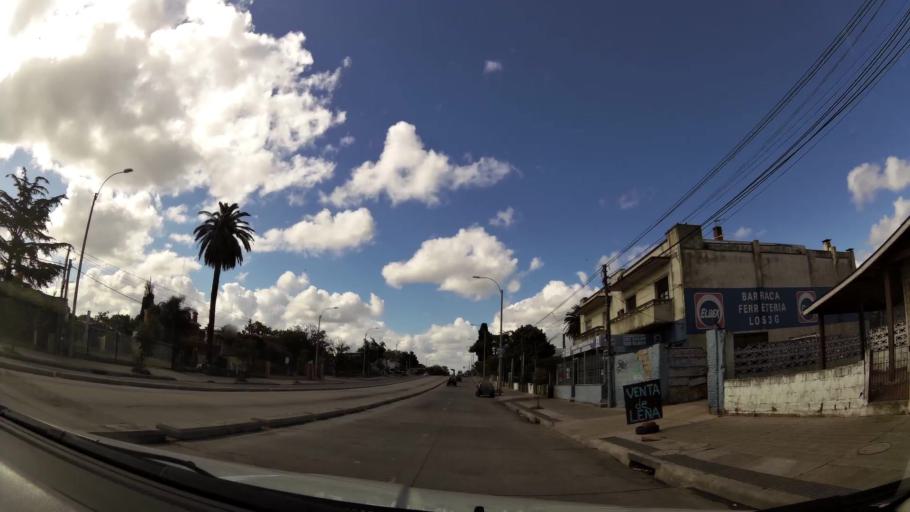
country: UY
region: Canelones
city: La Paz
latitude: -34.8176
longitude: -56.2202
